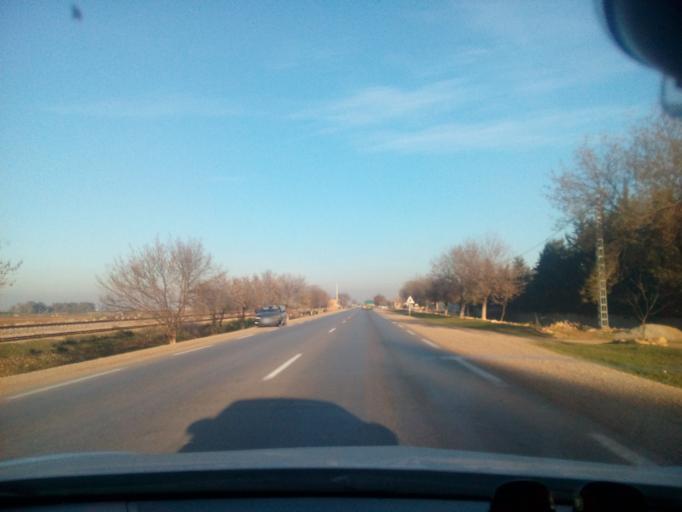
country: DZ
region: Chlef
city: Boukadir
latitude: 36.0481
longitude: 1.0864
